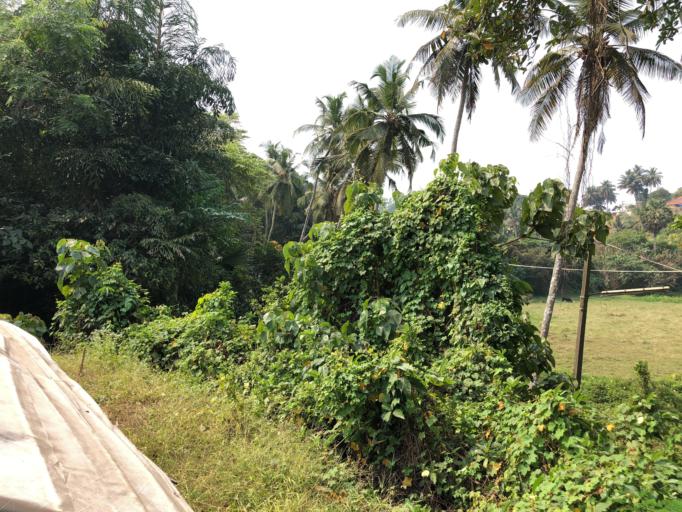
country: IN
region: Karnataka
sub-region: Dakshina Kannada
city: Mangalore
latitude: 12.8685
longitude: 74.8924
